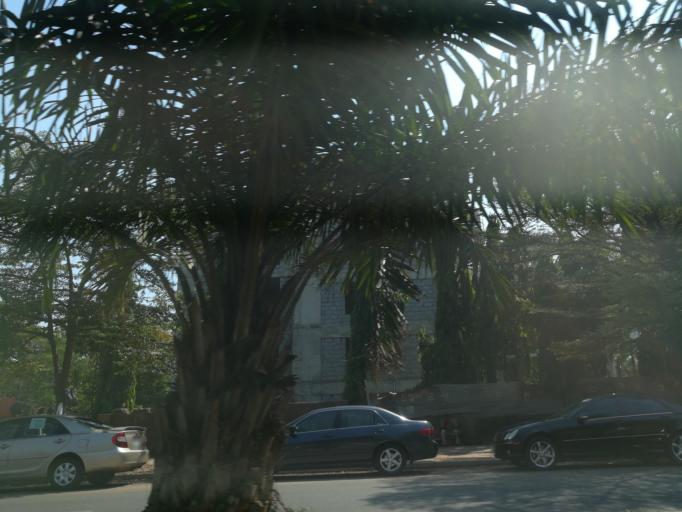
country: NG
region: Abuja Federal Capital Territory
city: Abuja
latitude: 9.0721
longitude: 7.4362
